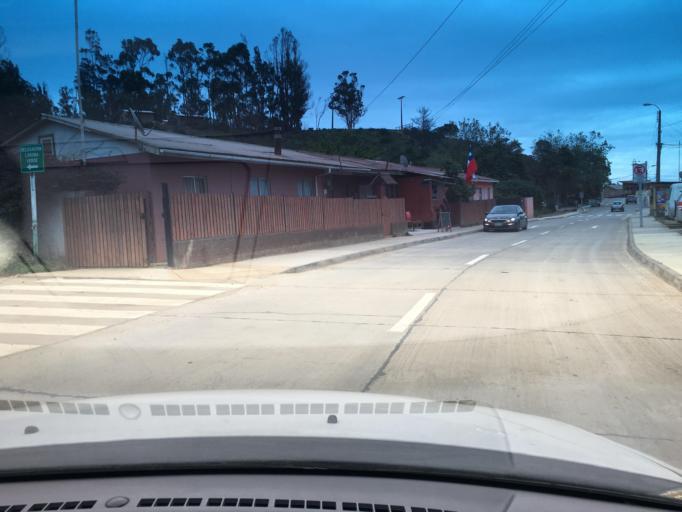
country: CL
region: Valparaiso
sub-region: Provincia de Valparaiso
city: Valparaiso
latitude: -33.1044
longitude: -71.6685
